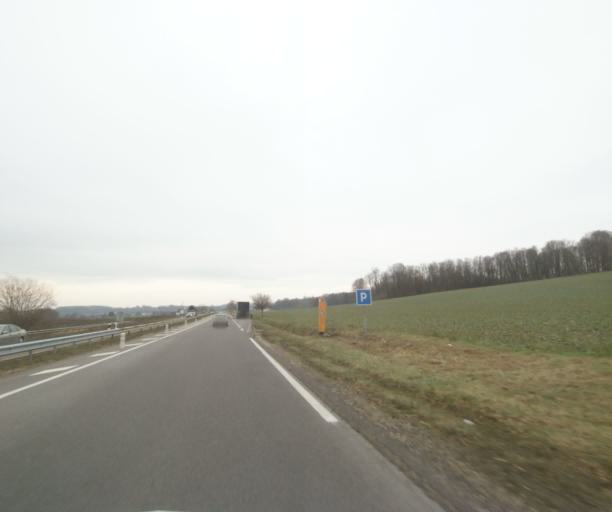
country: FR
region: Lorraine
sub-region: Departement de la Meuse
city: Ancerville
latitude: 48.6082
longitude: 5.0157
